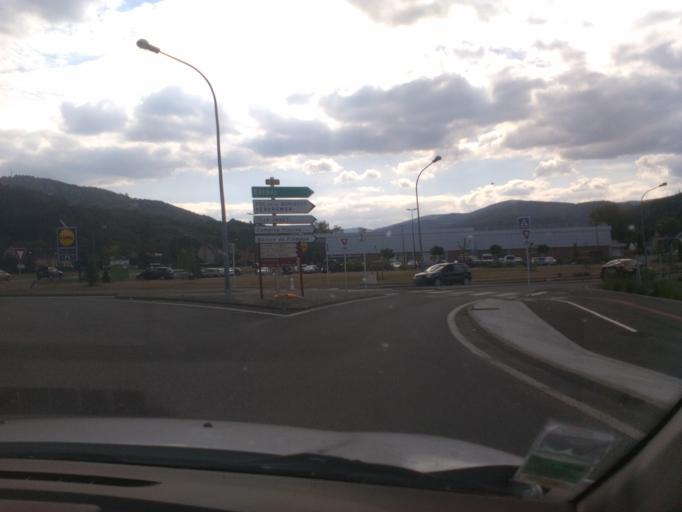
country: FR
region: Alsace
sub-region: Departement du Haut-Rhin
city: Munster
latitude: 48.0425
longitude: 7.1599
